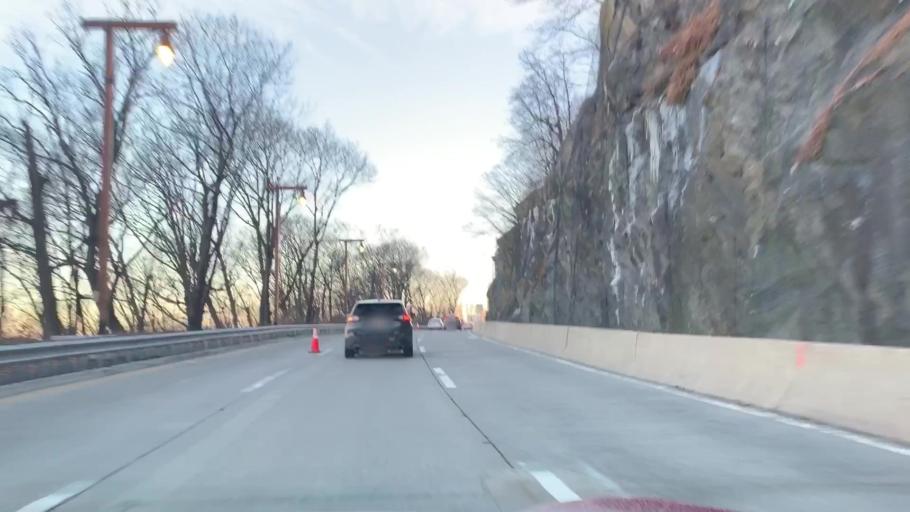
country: US
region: New York
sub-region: New York County
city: Inwood
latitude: 40.8736
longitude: -73.9276
